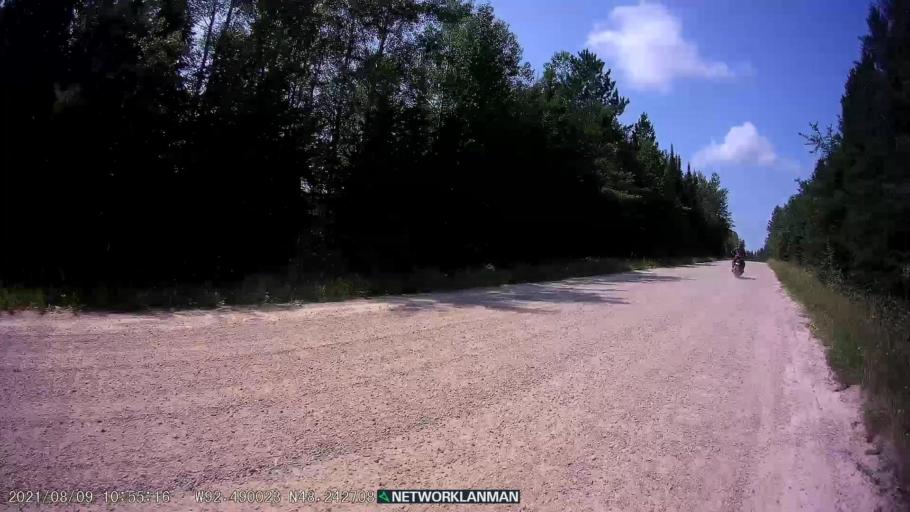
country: US
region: Minnesota
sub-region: Saint Louis County
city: Ely
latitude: 48.2426
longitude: -92.4904
